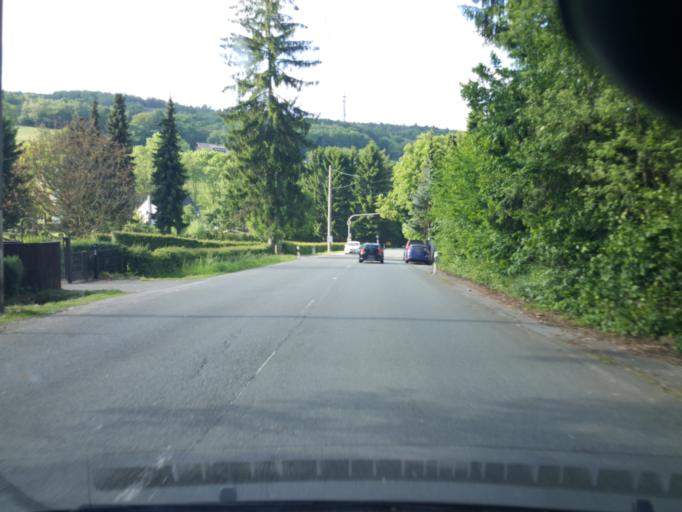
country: DE
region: North Rhine-Westphalia
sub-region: Regierungsbezirk Arnsberg
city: Hagen
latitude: 51.3298
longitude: 7.4677
